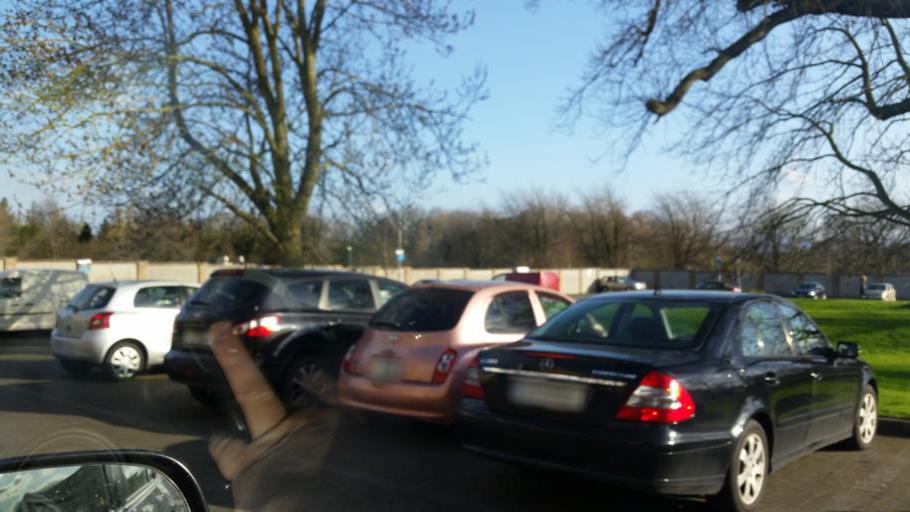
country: IE
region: Leinster
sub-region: Fingal County
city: Blanchardstown
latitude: 53.3916
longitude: -6.3666
